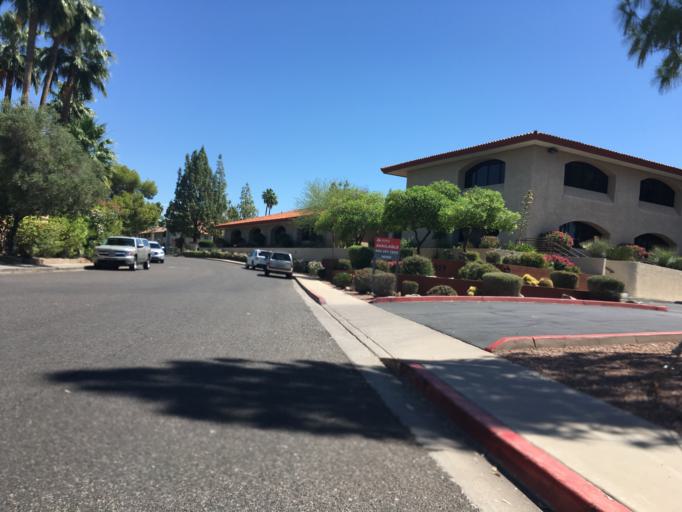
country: US
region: Arizona
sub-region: Maricopa County
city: Phoenix
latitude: 33.5448
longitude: -112.0432
